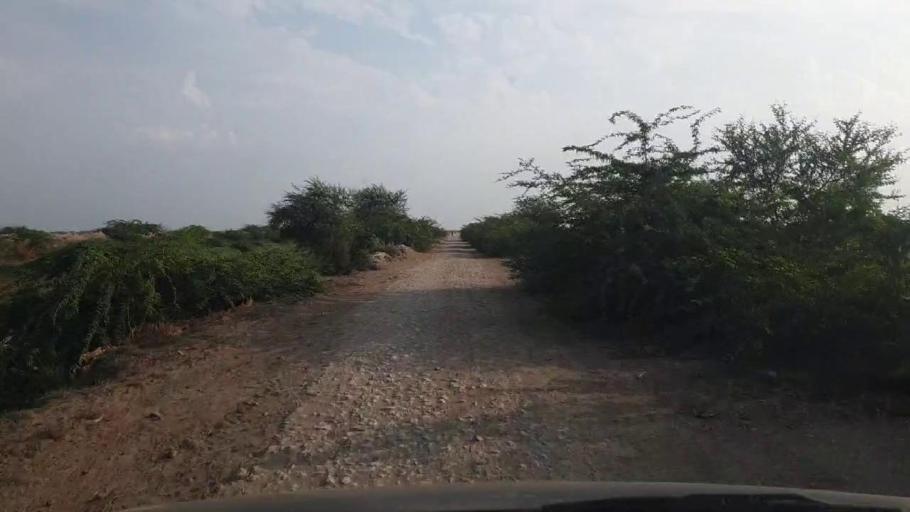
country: PK
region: Sindh
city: Badin
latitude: 24.5647
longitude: 68.6677
